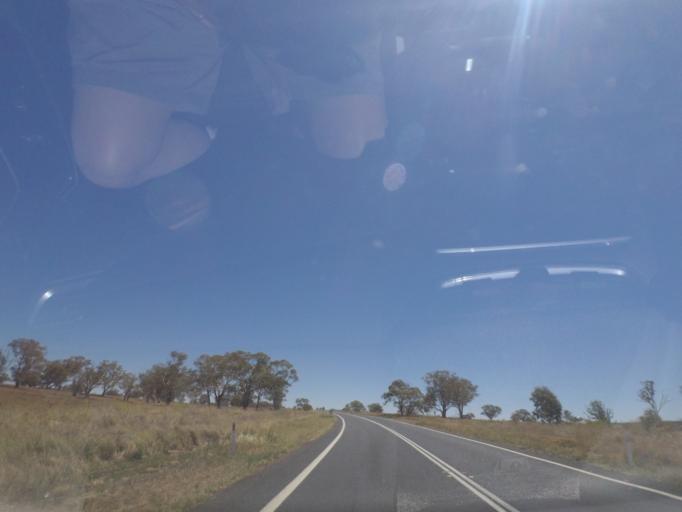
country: AU
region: New South Wales
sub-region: Warrumbungle Shire
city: Coonabarabran
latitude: -31.4380
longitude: 149.0426
